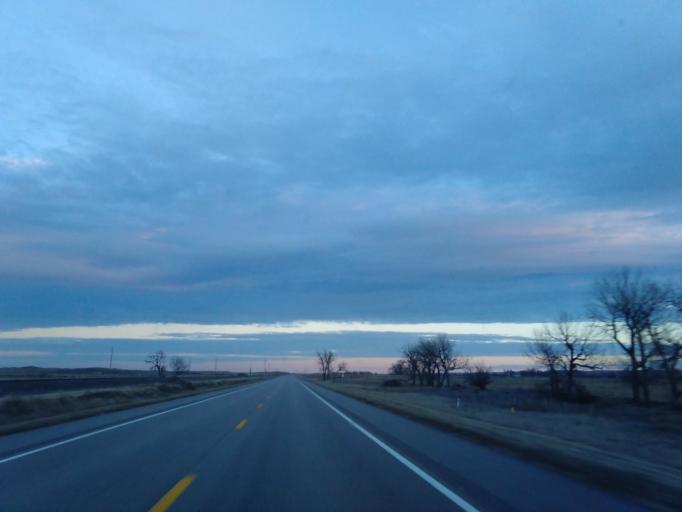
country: US
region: Nebraska
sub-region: Garden County
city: Oshkosh
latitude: 41.3888
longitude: -102.2938
